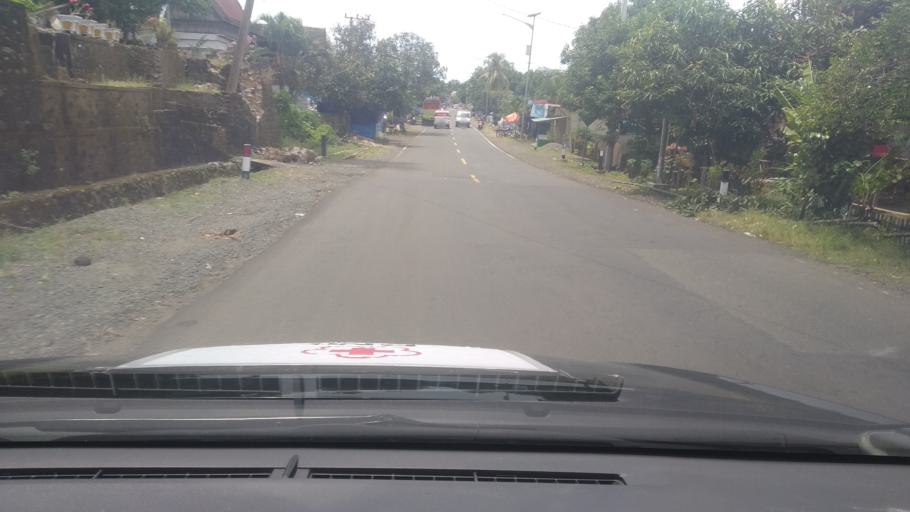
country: ID
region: Sulawesi Barat
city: Tapalang
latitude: -2.8451
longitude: 118.8608
